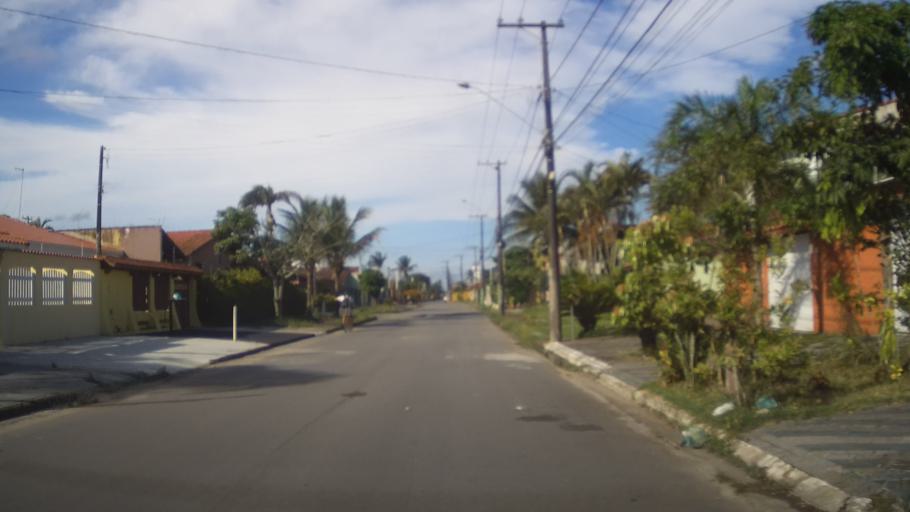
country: BR
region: Sao Paulo
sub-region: Itanhaem
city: Itanhaem
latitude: -24.1605
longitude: -46.7444
